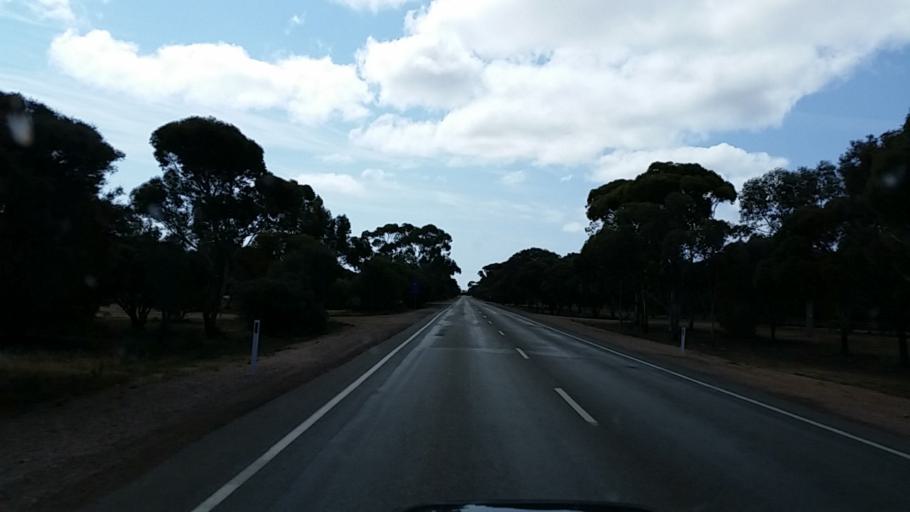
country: AU
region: South Australia
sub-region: Port Pirie City and Dists
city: Solomontown
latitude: -33.2223
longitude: 138.0121
